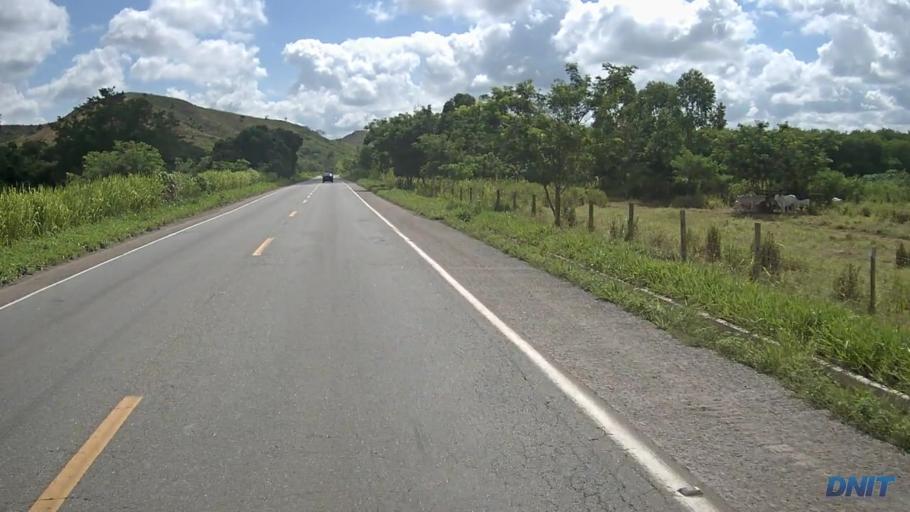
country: BR
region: Minas Gerais
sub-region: Belo Oriente
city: Belo Oriente
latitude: -19.1413
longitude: -42.2235
